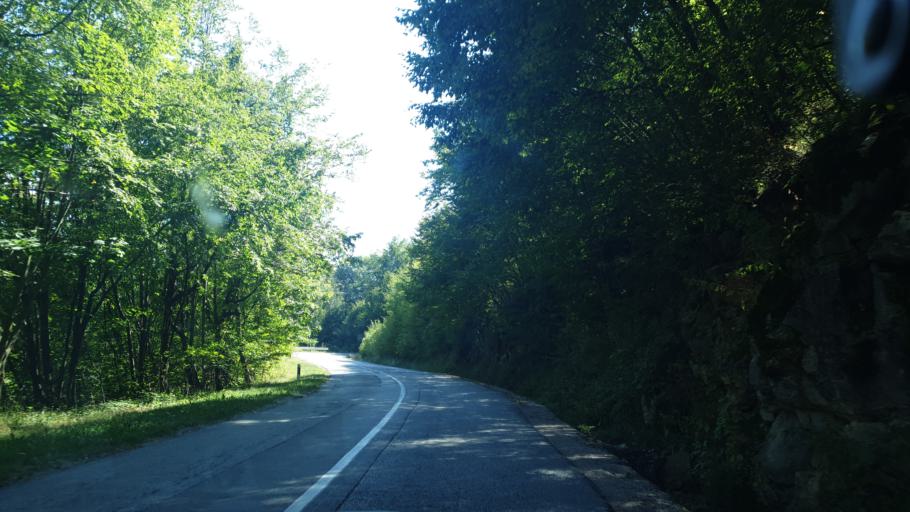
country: RS
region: Central Serbia
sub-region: Kolubarski Okrug
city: Mionica
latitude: 44.1504
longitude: 20.0212
